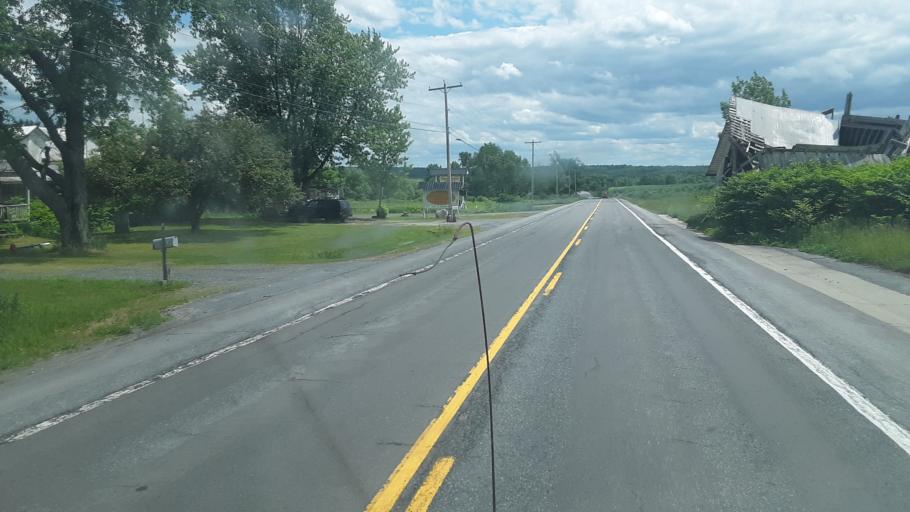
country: US
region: New York
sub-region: Oneida County
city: Rome
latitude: 43.3863
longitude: -75.4878
